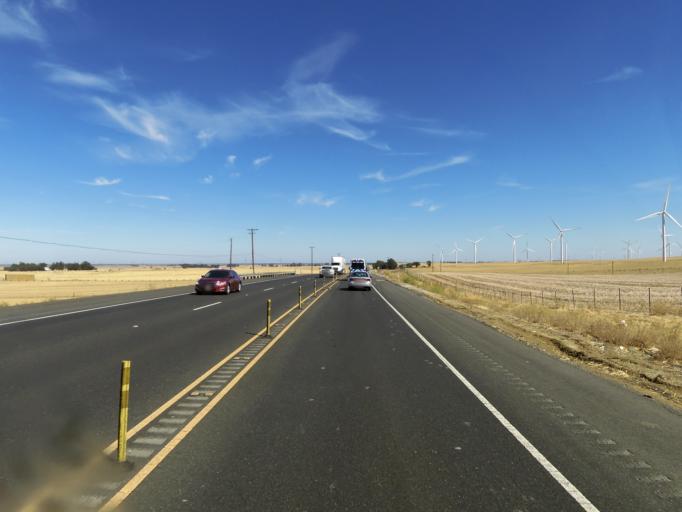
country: US
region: California
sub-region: Solano County
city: Rio Vista
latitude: 38.1835
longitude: -121.7819
